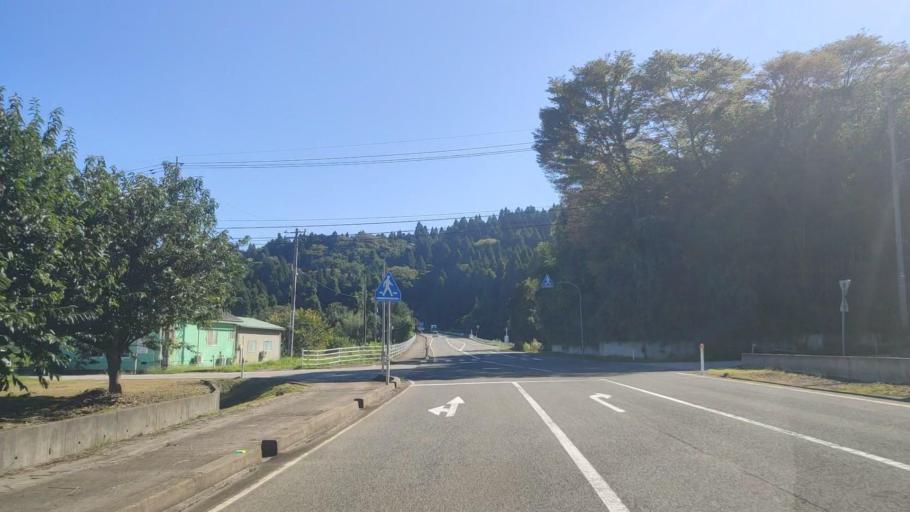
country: JP
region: Ishikawa
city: Nanao
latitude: 37.3871
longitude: 137.2329
